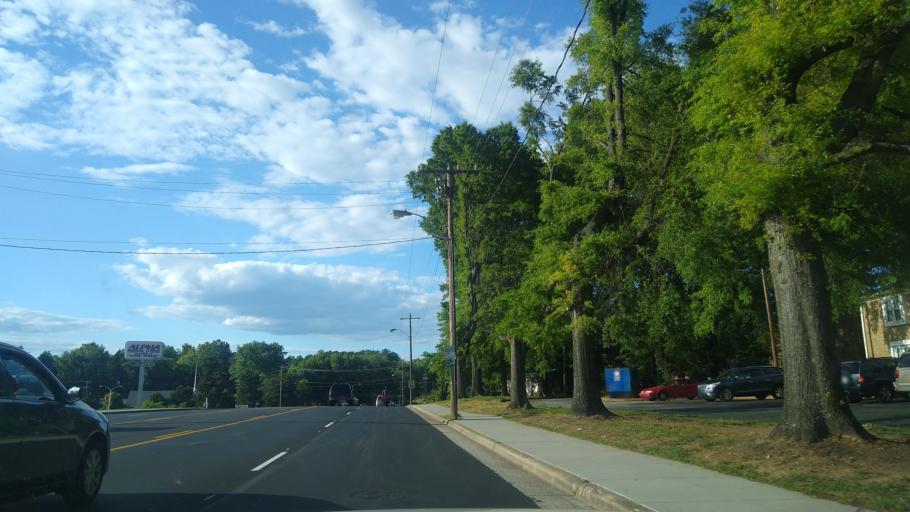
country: US
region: North Carolina
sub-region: Guilford County
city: Greensboro
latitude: 36.1150
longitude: -79.7750
